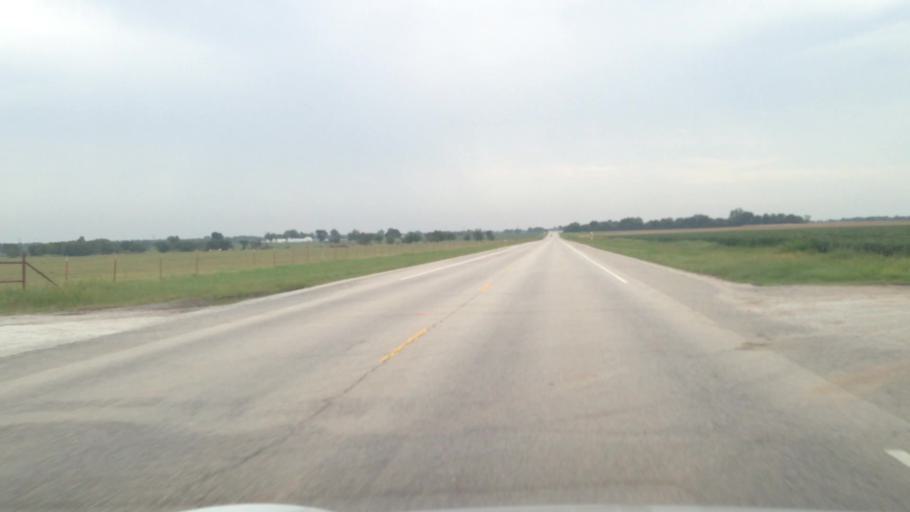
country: US
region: Oklahoma
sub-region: Ottawa County
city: Afton
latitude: 36.6417
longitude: -94.9815
